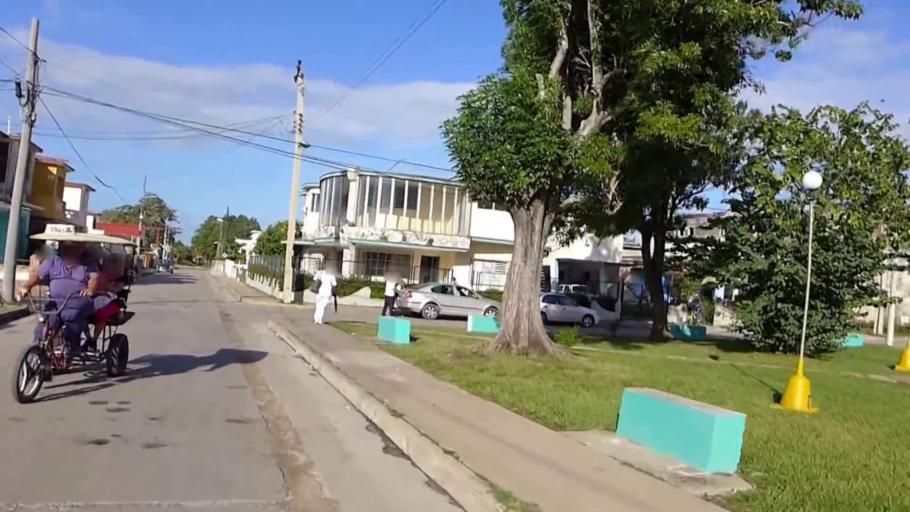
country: CU
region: Camaguey
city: Camaguey
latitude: 21.3866
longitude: -77.9231
